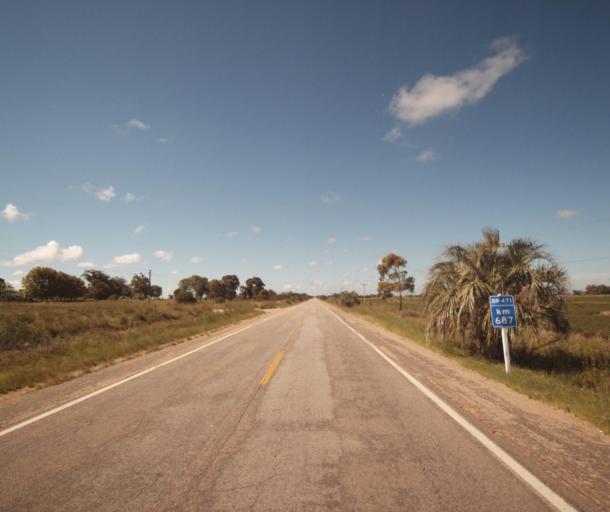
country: BR
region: Rio Grande do Sul
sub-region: Chui
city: Chui
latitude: -33.6458
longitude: -53.4251
